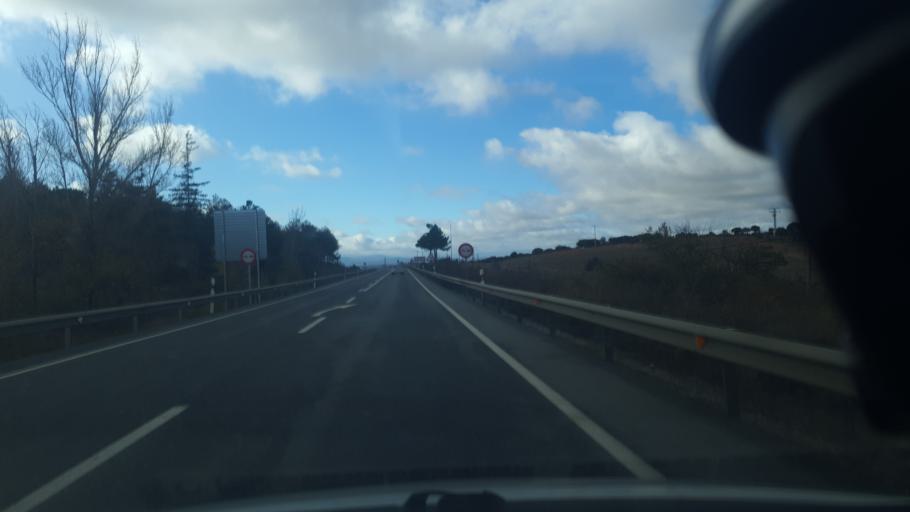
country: ES
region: Castille and Leon
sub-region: Provincia de Avila
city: Ojos-Albos
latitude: 40.7356
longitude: -4.4953
